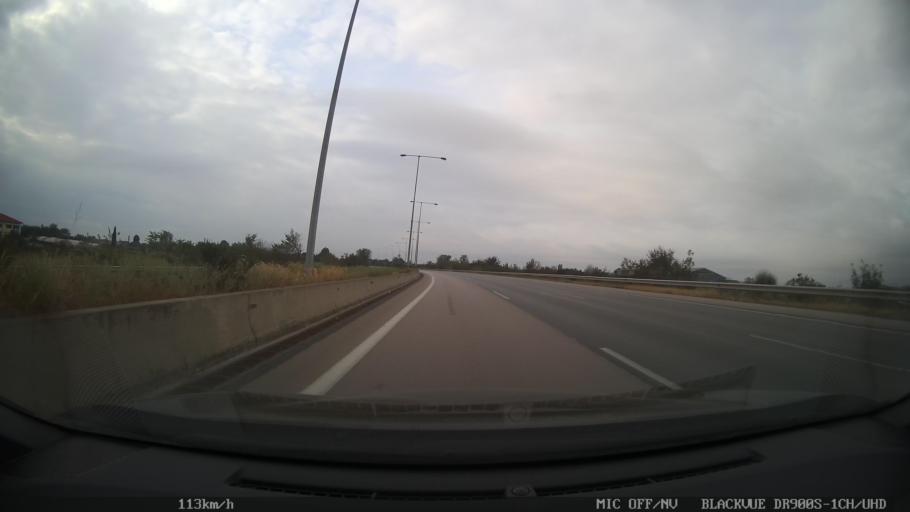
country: GR
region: Central Macedonia
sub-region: Nomos Thessalonikis
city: Nea Magnisia
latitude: 40.6884
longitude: 22.8349
